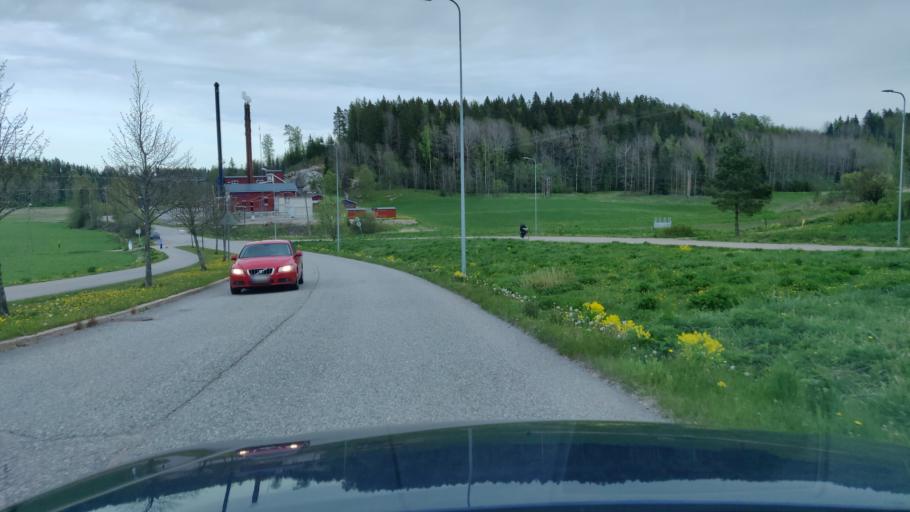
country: FI
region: Uusimaa
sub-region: Helsinki
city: Nurmijaervi
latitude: 60.3845
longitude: 24.7607
